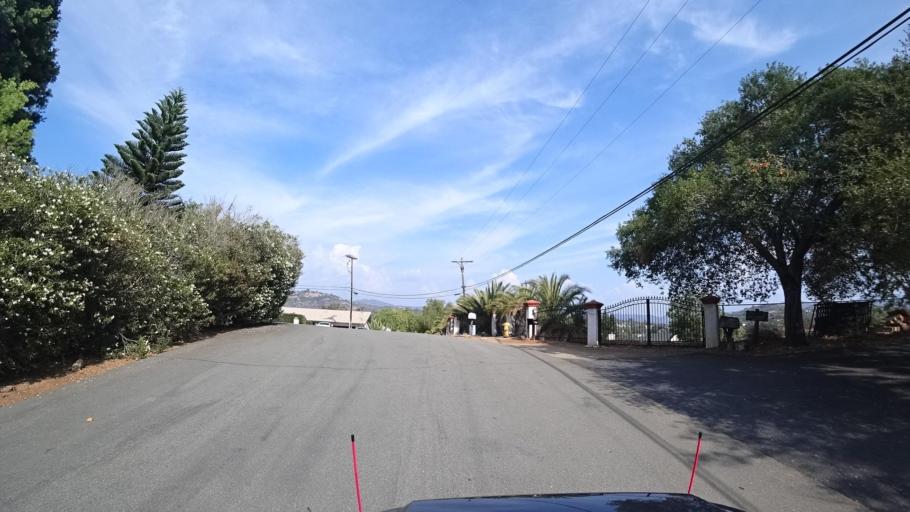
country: US
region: California
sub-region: San Diego County
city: Escondido
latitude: 33.1113
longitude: -117.0539
